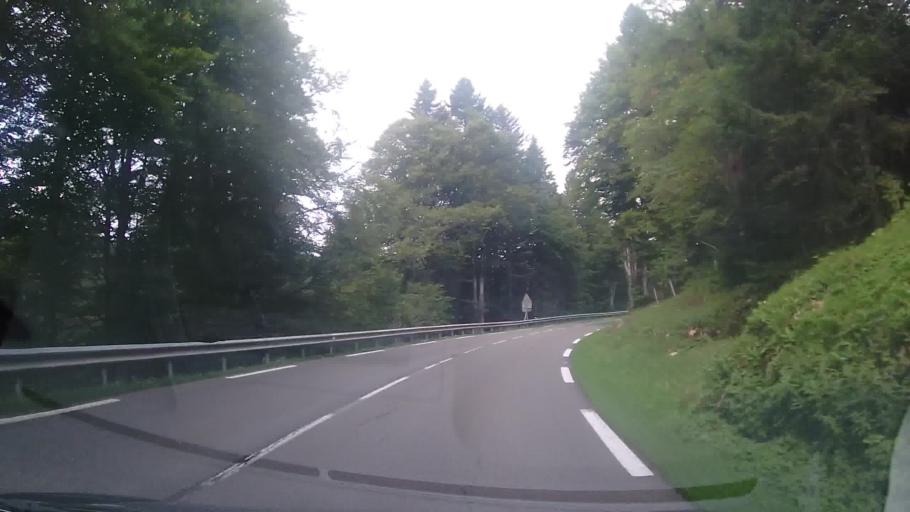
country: FR
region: Franche-Comte
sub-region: Departement du Jura
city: Les Rousses
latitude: 46.4162
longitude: 6.0621
